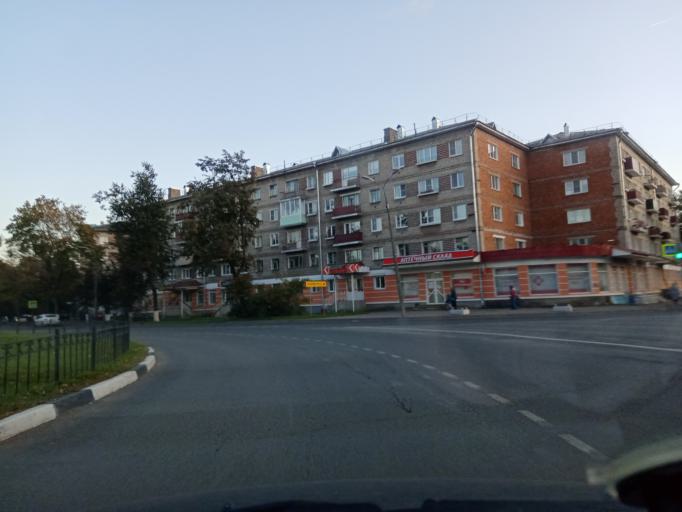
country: RU
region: Pskov
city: Pskov
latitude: 57.8077
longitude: 28.3394
